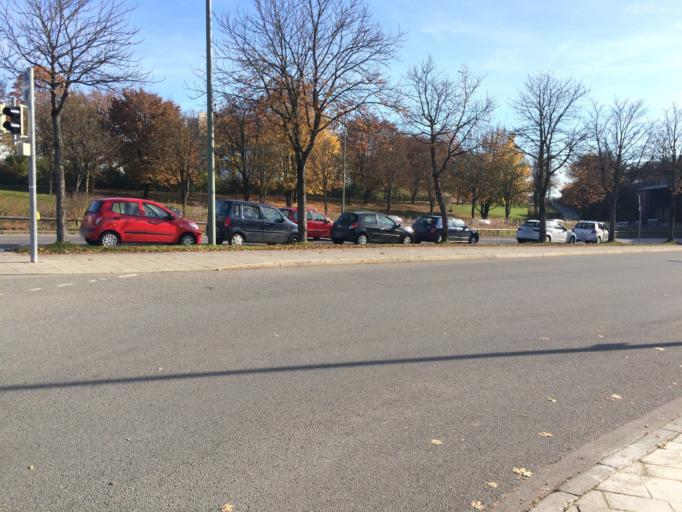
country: DE
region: Bavaria
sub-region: Upper Bavaria
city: Neubiberg
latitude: 48.0899
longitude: 11.6447
